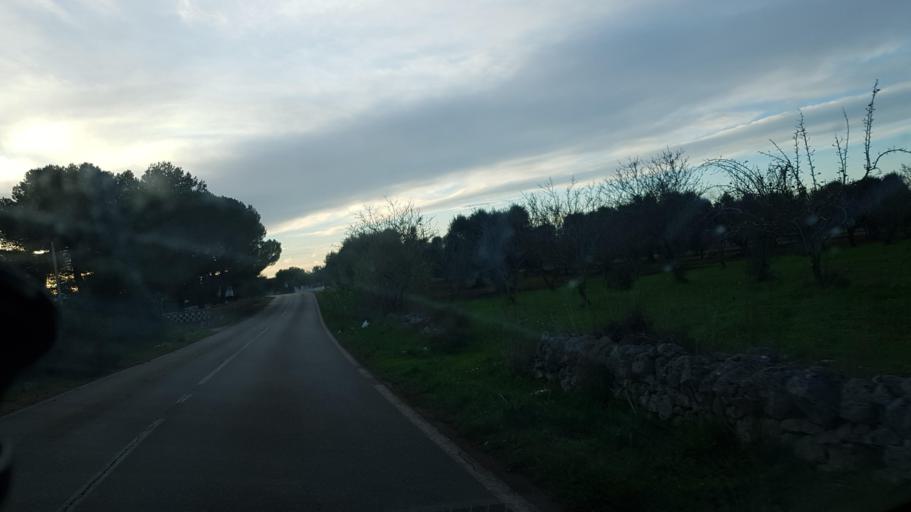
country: IT
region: Apulia
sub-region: Provincia di Brindisi
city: San Michele Salentino
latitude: 40.6471
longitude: 17.6651
